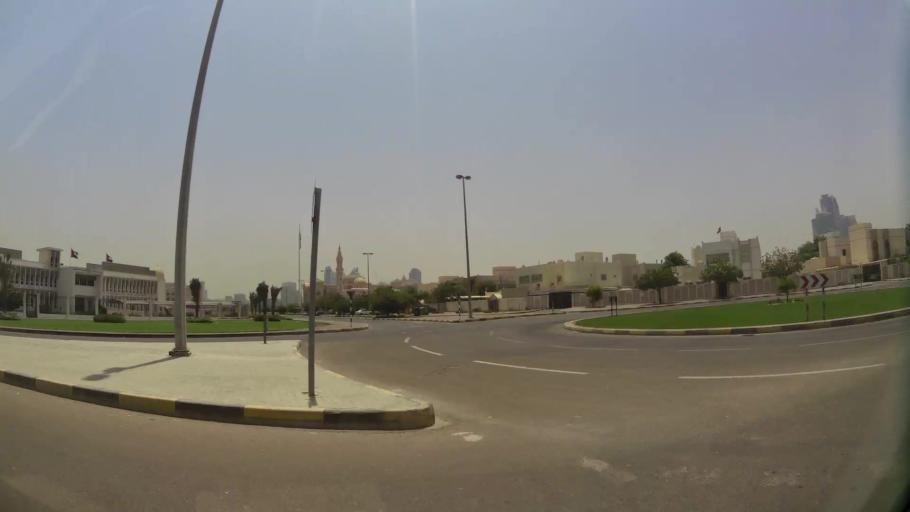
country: AE
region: Ash Shariqah
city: Sharjah
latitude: 25.3467
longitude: 55.3718
